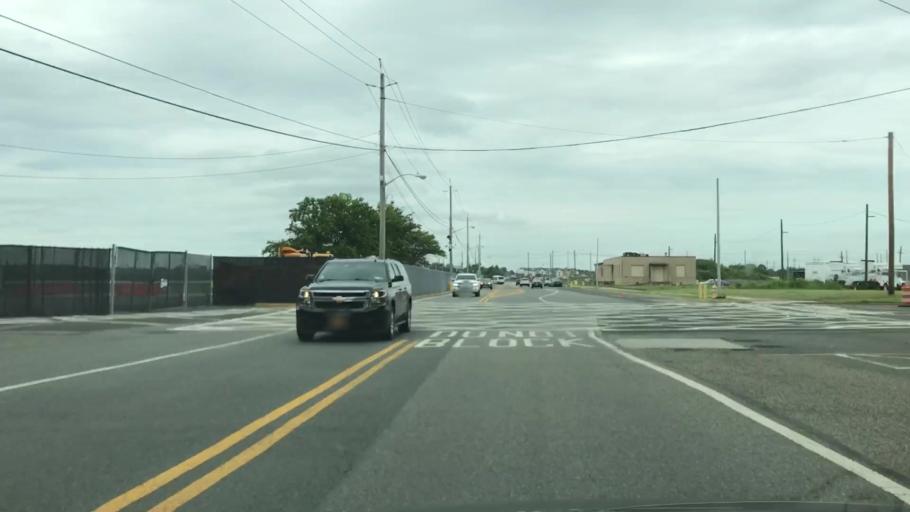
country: US
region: New Jersey
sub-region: Hudson County
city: Bayonne
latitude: 40.6667
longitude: -74.0844
